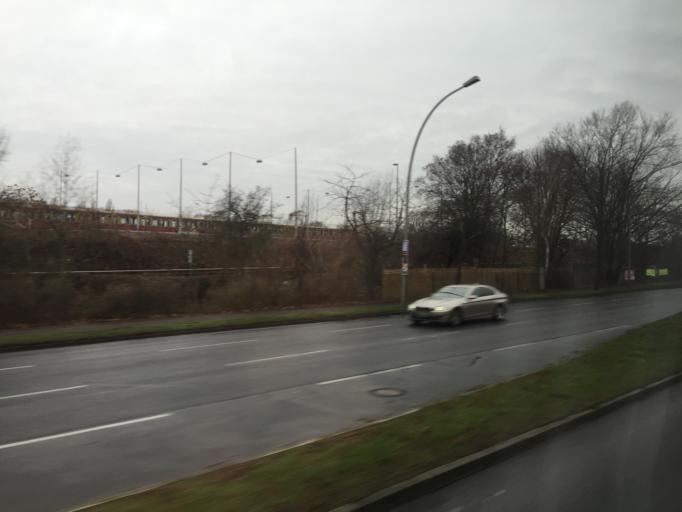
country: DE
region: Berlin
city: Niederschoneweide
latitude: 52.4505
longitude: 13.5193
